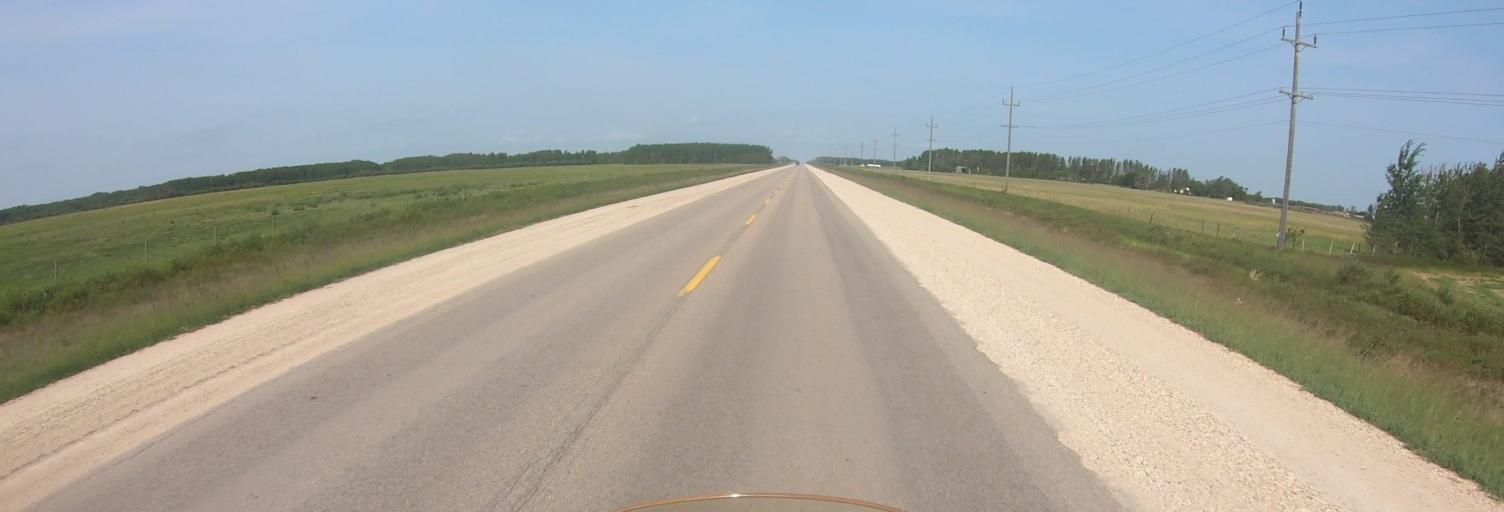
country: CA
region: Manitoba
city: La Broquerie
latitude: 49.3000
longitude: -96.5441
